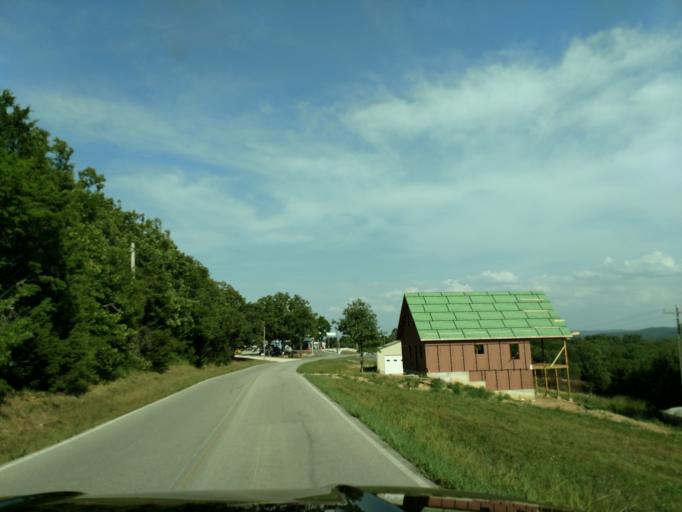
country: US
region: Missouri
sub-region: Barry County
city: Shell Knob
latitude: 36.6073
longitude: -93.5686
